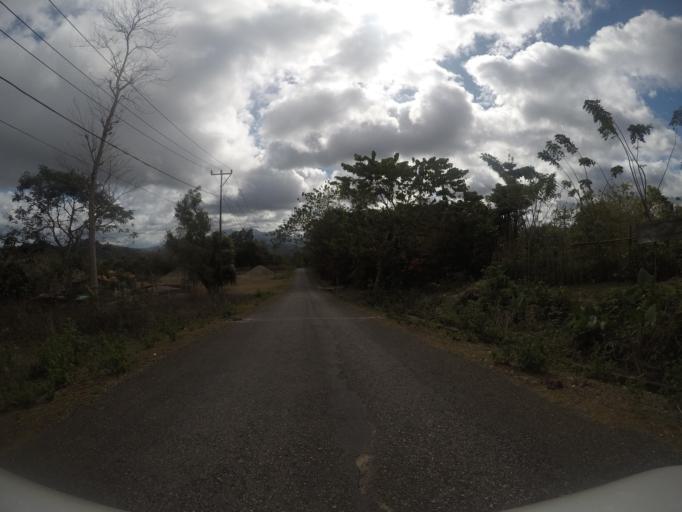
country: TL
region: Lautem
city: Lospalos
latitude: -8.5374
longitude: 126.9117
